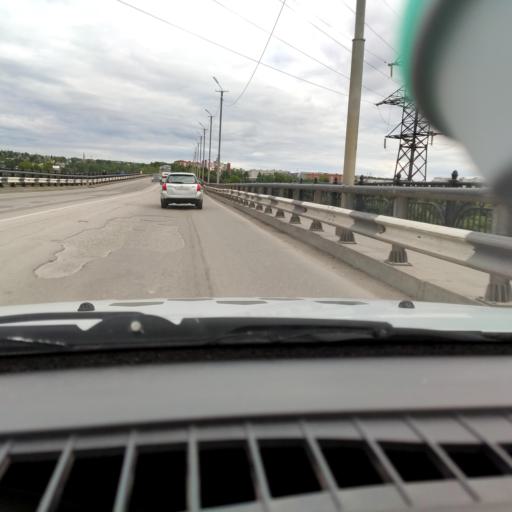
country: RU
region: Perm
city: Chusovoy
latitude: 58.2883
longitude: 57.8122
